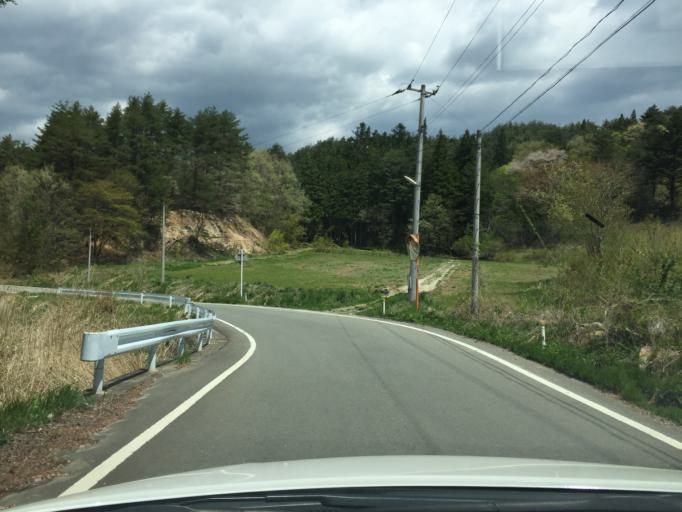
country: JP
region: Fukushima
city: Yanagawamachi-saiwaicho
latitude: 37.6951
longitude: 140.6763
